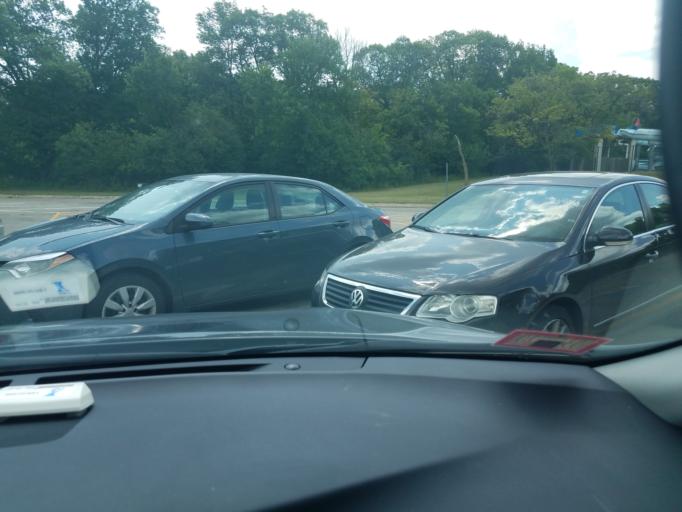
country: US
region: Illinois
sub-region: Cook County
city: Niles
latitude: 41.9995
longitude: -87.7826
